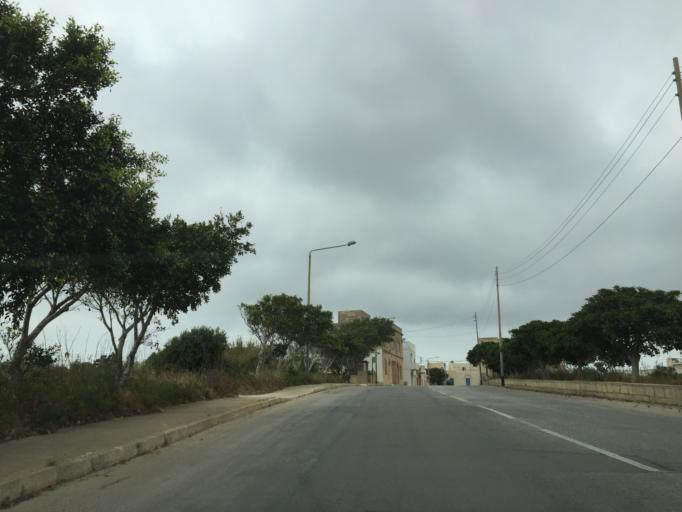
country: MT
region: L-Imgarr
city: Imgarr
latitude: 35.9261
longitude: 14.3682
